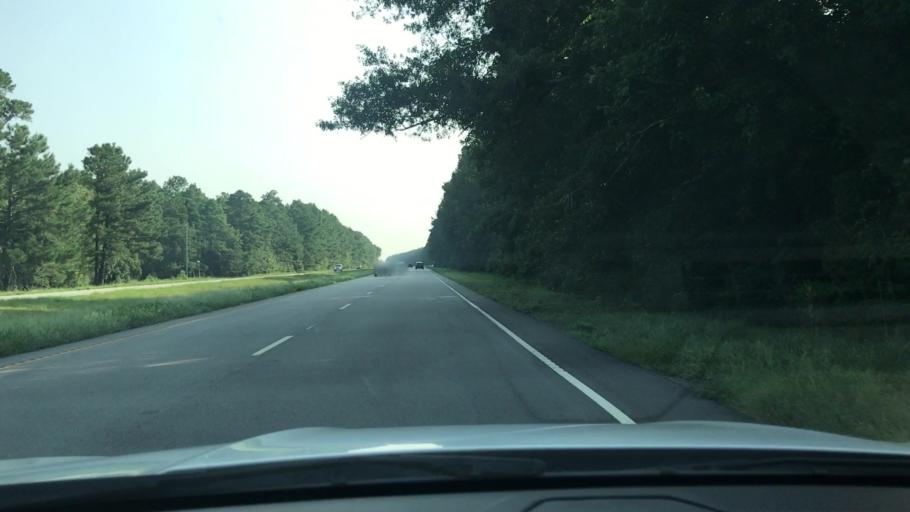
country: US
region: South Carolina
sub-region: Charleston County
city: Awendaw
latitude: 33.1162
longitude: -79.4560
